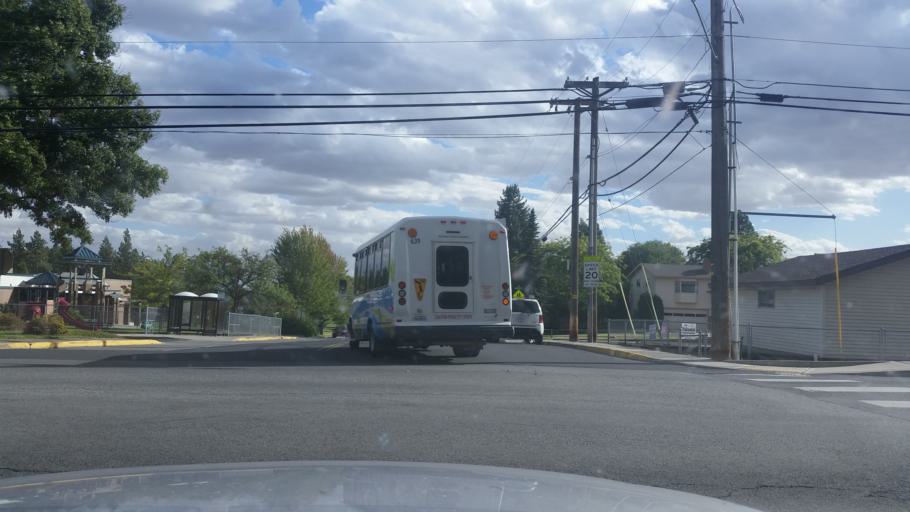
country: US
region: Washington
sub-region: Spokane County
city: Cheney
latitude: 47.4820
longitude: -117.5968
